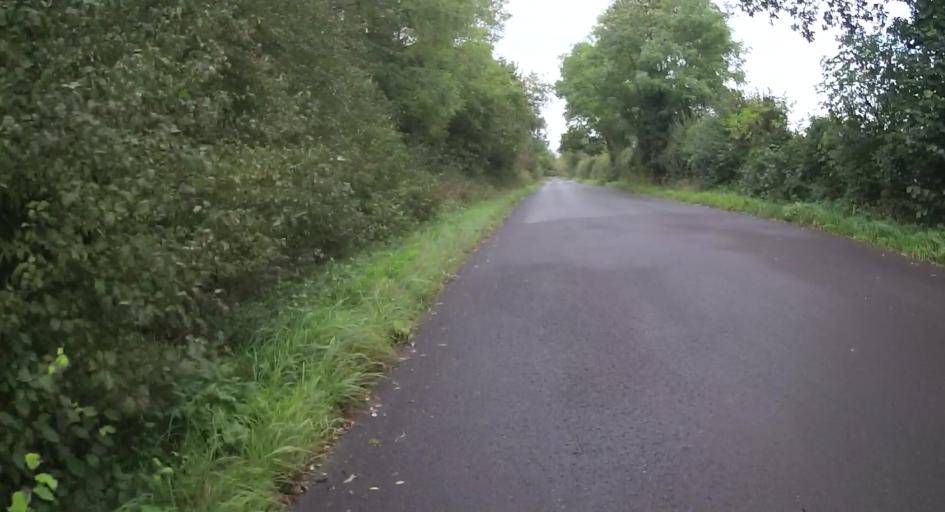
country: GB
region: England
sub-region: Hampshire
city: Tadley
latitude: 51.3872
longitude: -1.1782
